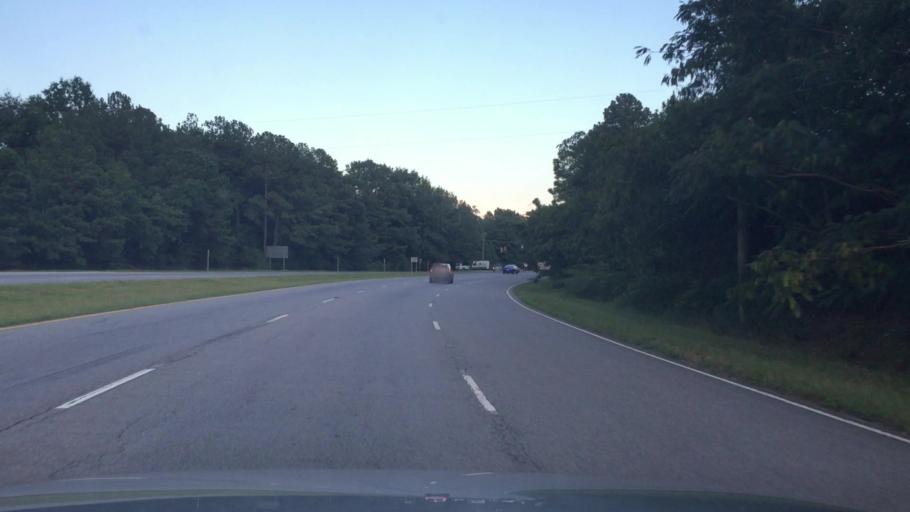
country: US
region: South Carolina
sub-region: Richland County
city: Forest Acres
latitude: 33.9495
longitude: -80.9672
